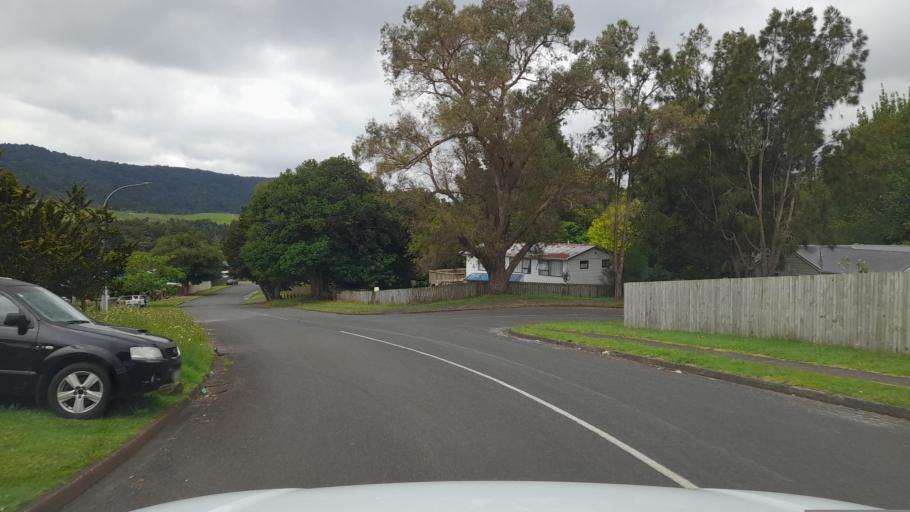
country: NZ
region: Northland
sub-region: Far North District
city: Waimate North
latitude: -35.4043
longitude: 173.7856
